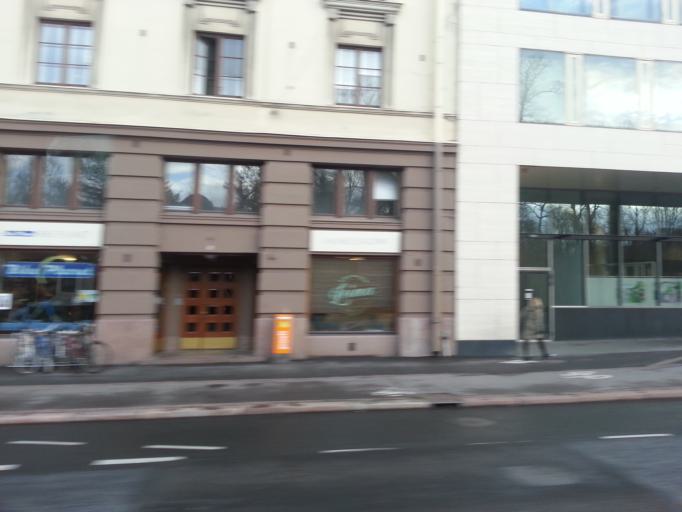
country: FI
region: Uusimaa
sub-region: Helsinki
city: Helsinki
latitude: 60.1753
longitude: 24.9502
